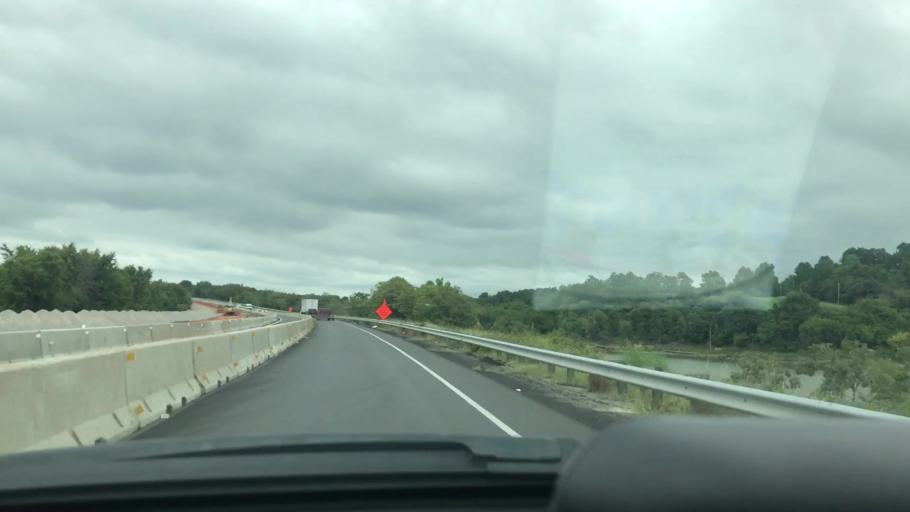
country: US
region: Oklahoma
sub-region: McIntosh County
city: Eufaula
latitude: 35.2467
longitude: -95.5851
